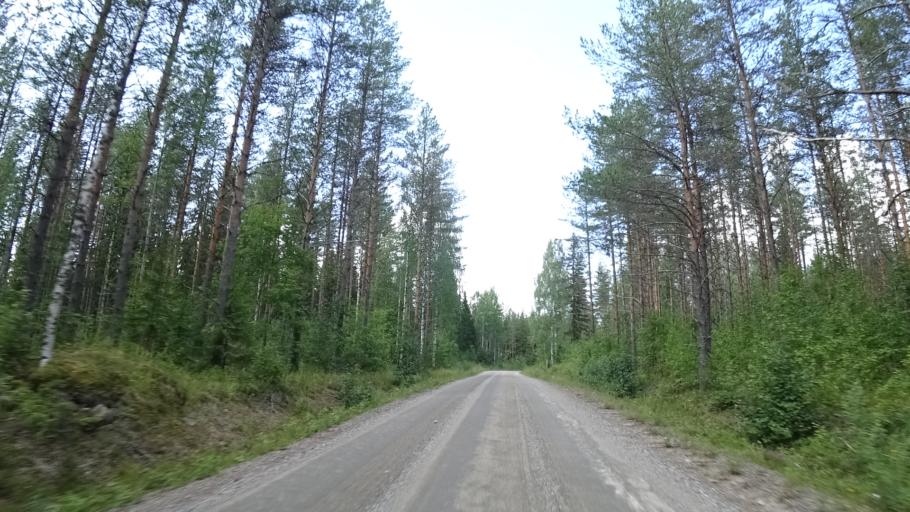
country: FI
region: North Karelia
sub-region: Joensuu
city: Ilomantsi
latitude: 62.9222
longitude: 31.3363
